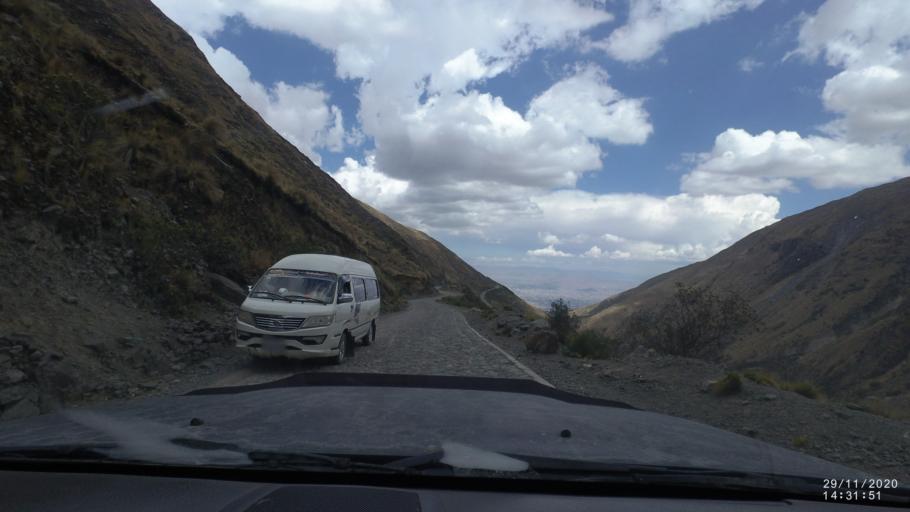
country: BO
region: Cochabamba
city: Sipe Sipe
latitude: -17.2661
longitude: -66.3427
